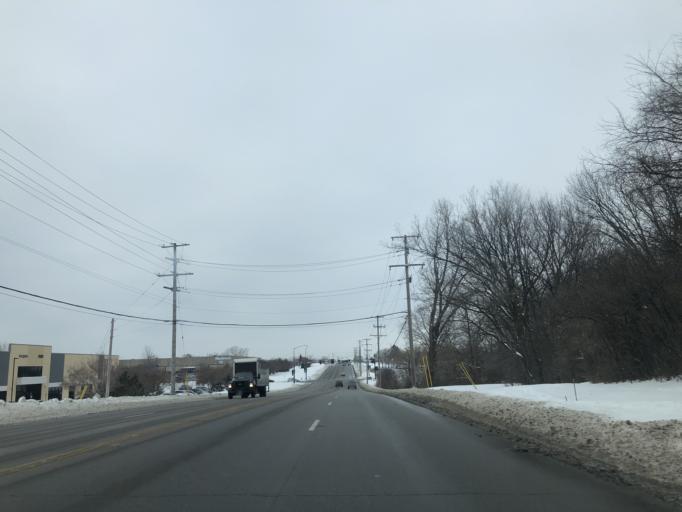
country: US
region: Minnesota
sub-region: Hennepin County
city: Osseo
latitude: 45.0946
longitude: -93.3932
